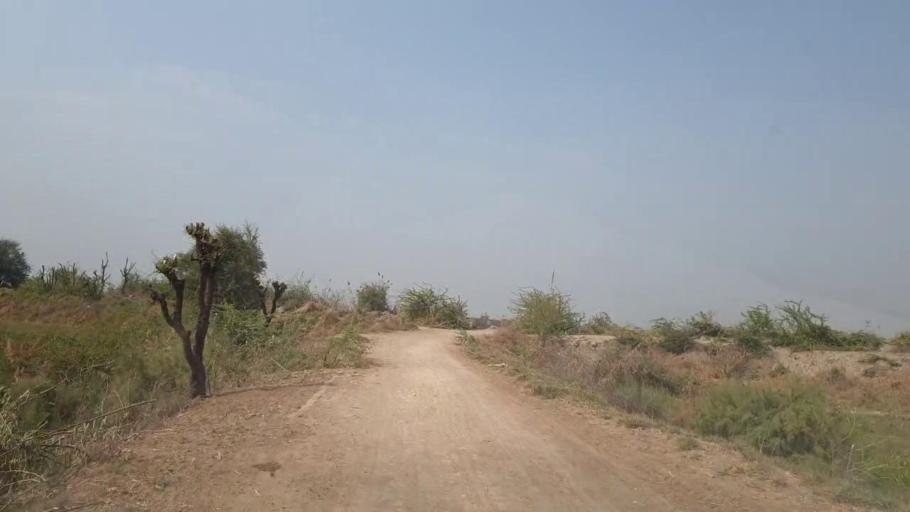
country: PK
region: Sindh
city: Mirpur Khas
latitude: 25.5746
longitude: 69.1359
